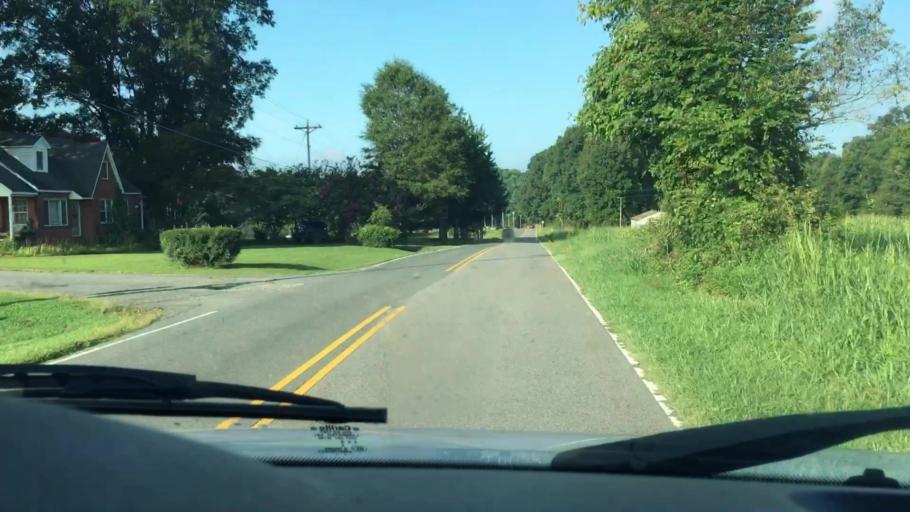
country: US
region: North Carolina
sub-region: Mecklenburg County
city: Huntersville
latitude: 35.4302
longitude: -80.8087
